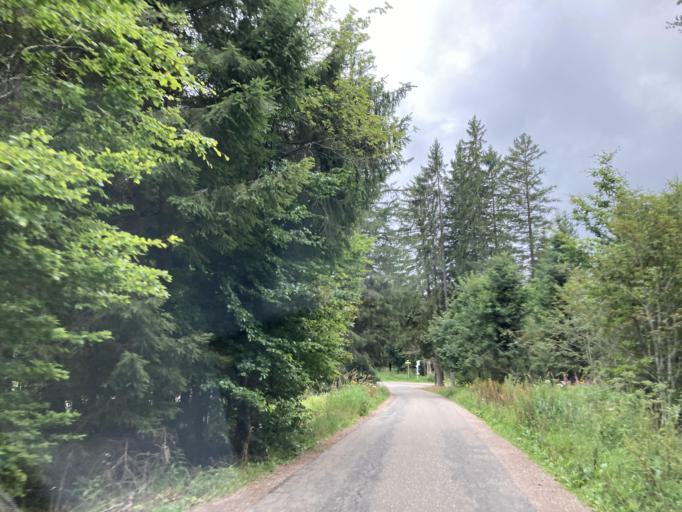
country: DE
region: Baden-Wuerttemberg
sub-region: Freiburg Region
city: Schonwald im Schwarzwald
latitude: 48.1098
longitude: 8.1721
